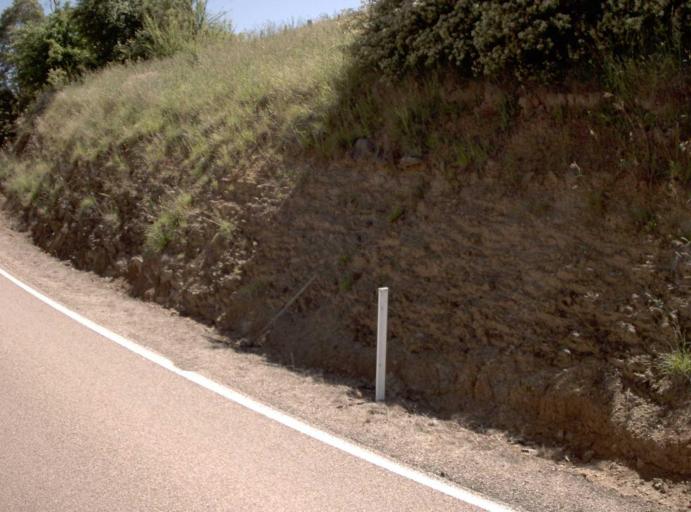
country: AU
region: Victoria
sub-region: East Gippsland
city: Lakes Entrance
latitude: -37.4919
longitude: 148.1726
